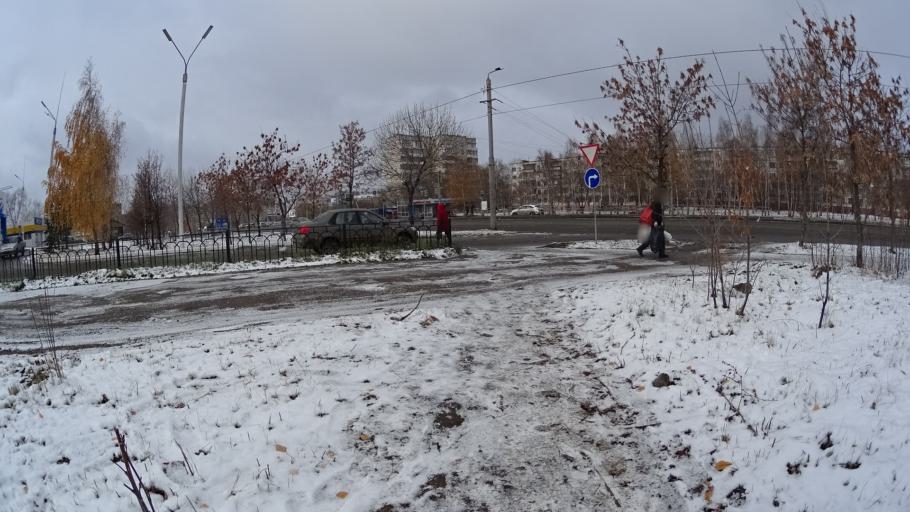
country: RU
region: Chelyabinsk
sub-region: Gorod Chelyabinsk
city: Chelyabinsk
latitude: 55.1884
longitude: 61.3101
